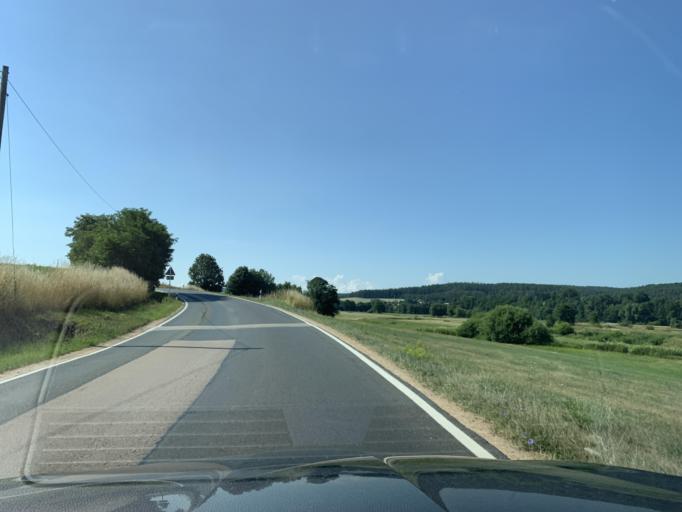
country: DE
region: Bavaria
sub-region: Upper Palatinate
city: Schwarzhofen
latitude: 49.3861
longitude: 12.3364
